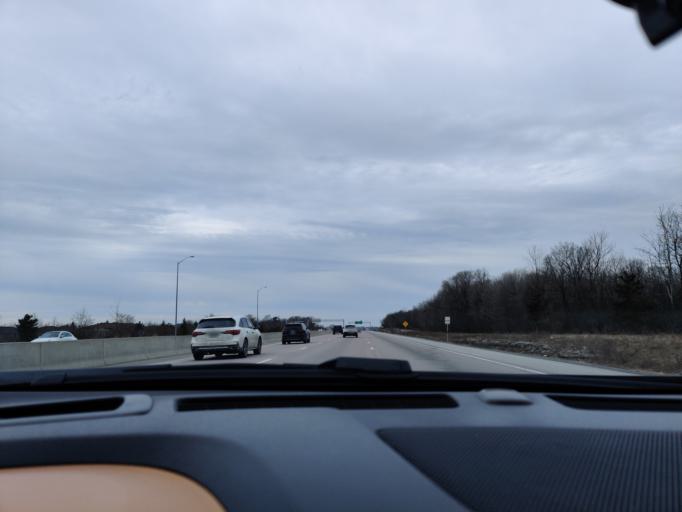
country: CA
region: Ontario
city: Kingston
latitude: 44.2739
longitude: -76.4829
